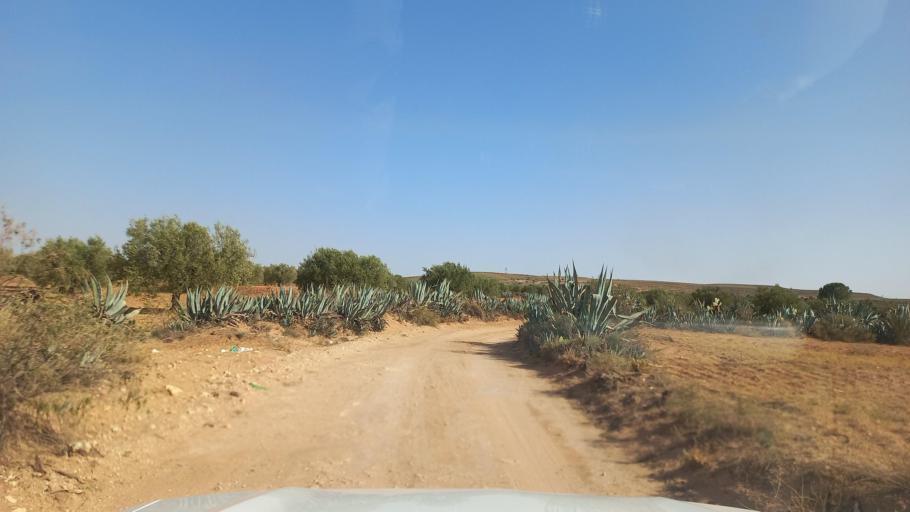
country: TN
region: Al Qasrayn
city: Kasserine
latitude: 35.2036
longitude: 8.9626
